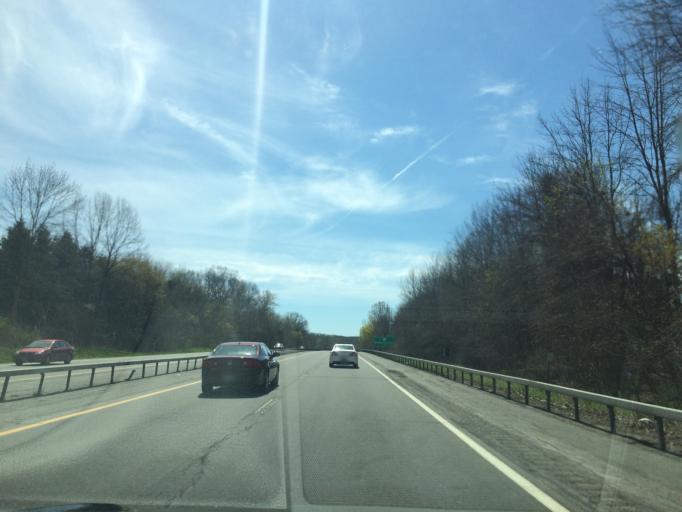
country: US
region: New York
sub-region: Monroe County
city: East Rochester
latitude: 43.0746
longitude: -77.4813
